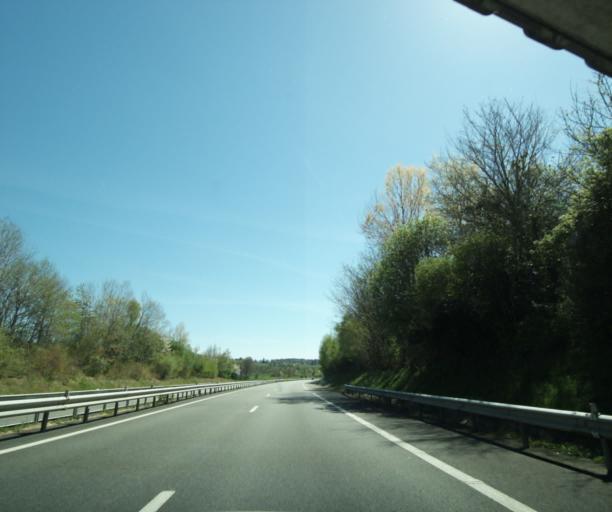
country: FR
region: Limousin
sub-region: Departement de la Haute-Vienne
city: Saint-Germain-les-Belles
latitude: 45.5545
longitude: 1.5062
